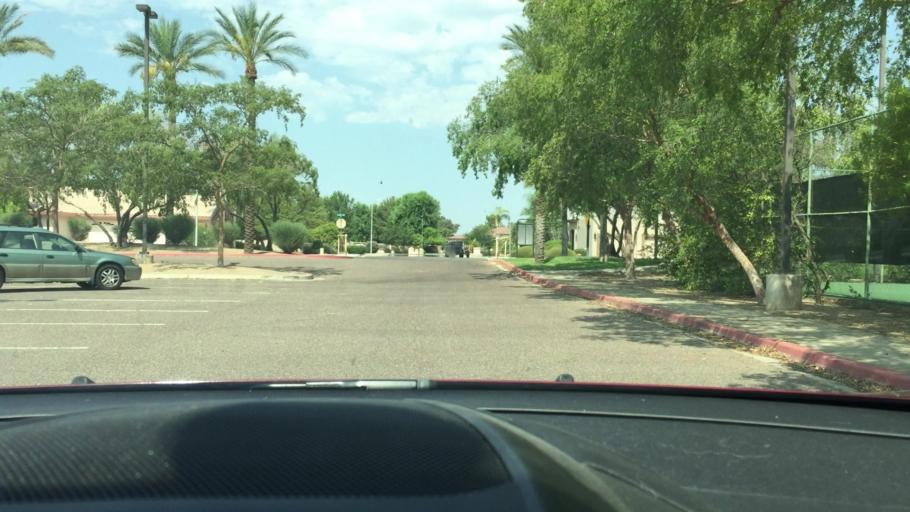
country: US
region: Arizona
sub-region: Maricopa County
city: Peoria
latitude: 33.6132
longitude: -112.1938
